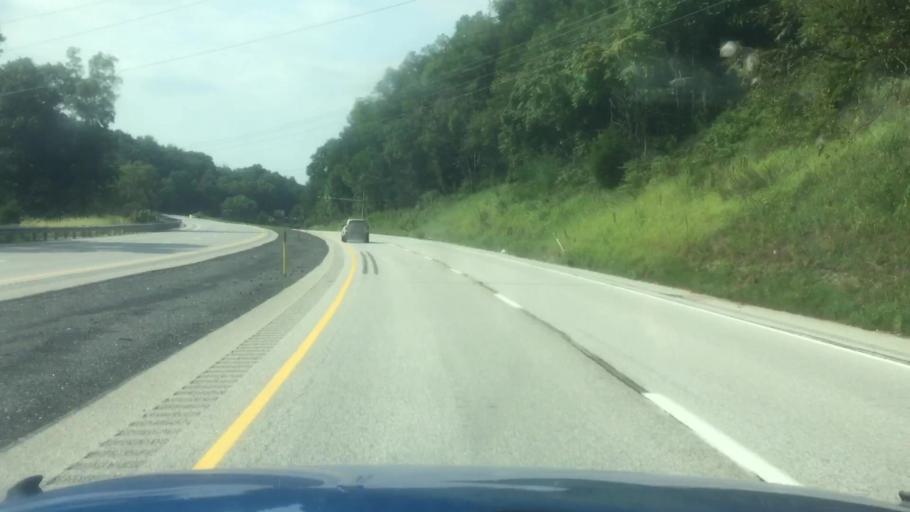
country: US
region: Pennsylvania
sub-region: York County
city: Grantley
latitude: 39.9402
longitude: -76.7149
